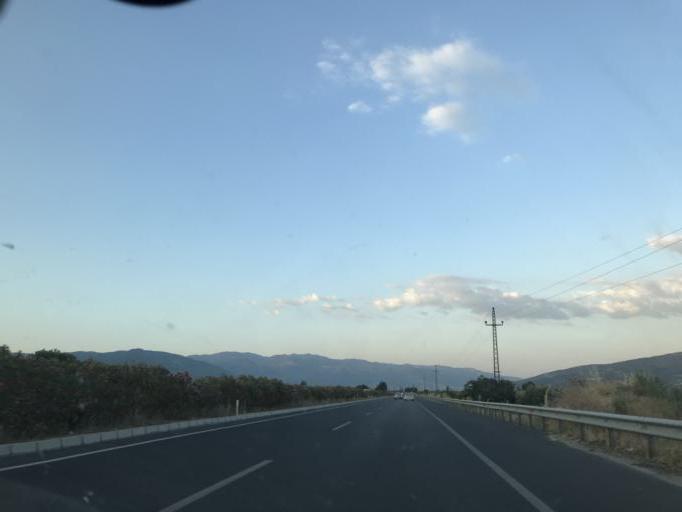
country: TR
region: Aydin
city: Horsunlu
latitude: 37.9246
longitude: 28.6475
